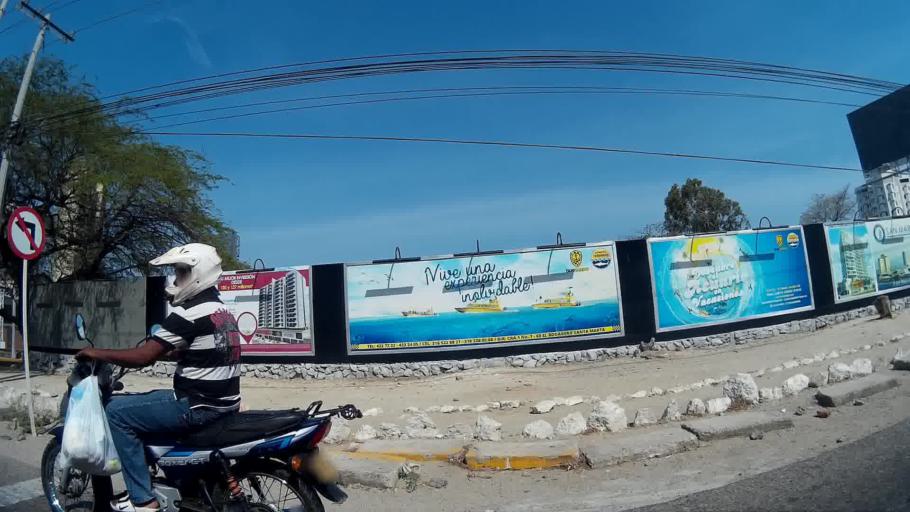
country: CO
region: Magdalena
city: Santa Marta
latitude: 11.2006
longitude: -74.2261
